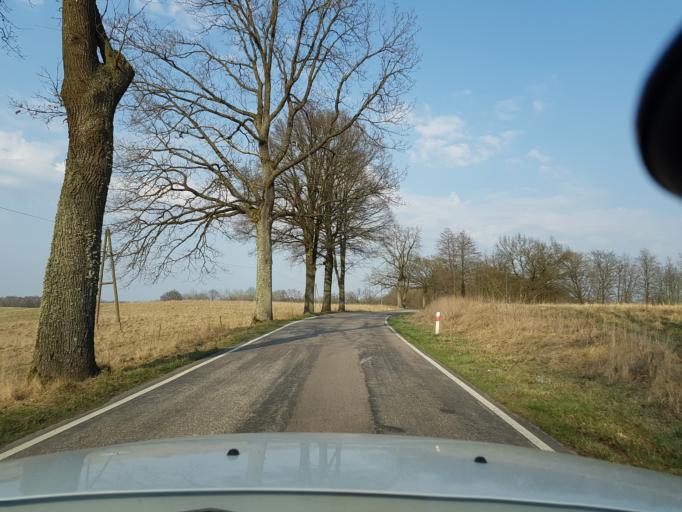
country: PL
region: West Pomeranian Voivodeship
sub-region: Powiat drawski
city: Drawsko Pomorskie
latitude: 53.5732
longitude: 15.8588
